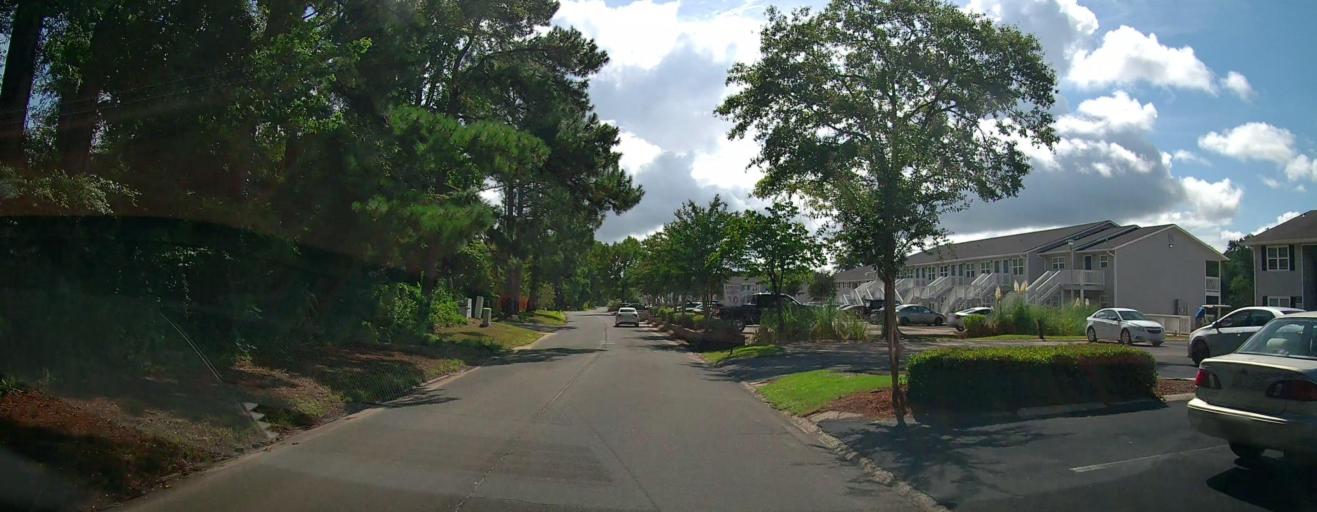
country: US
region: Georgia
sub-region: Houston County
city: Warner Robins
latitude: 32.5856
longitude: -83.6314
